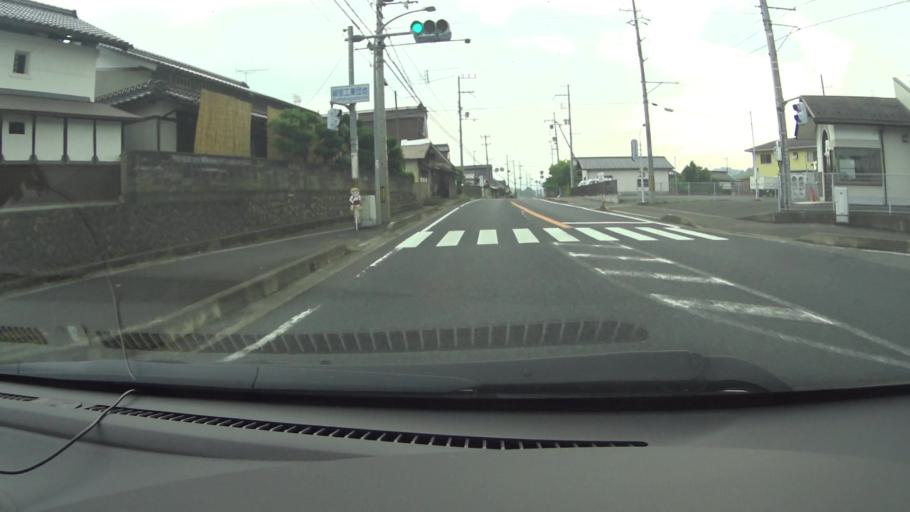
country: JP
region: Kyoto
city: Ayabe
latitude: 35.3239
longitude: 135.2909
